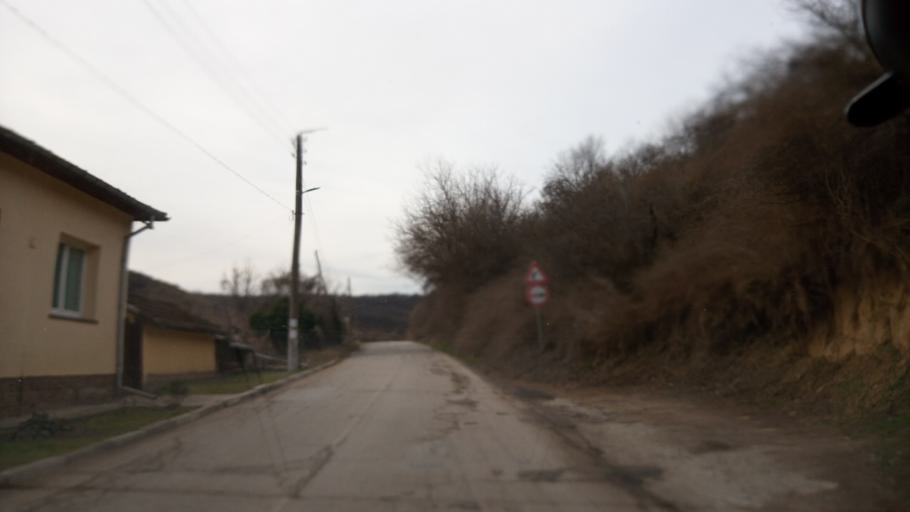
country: BG
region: Pleven
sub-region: Obshtina Belene
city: Belene
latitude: 43.5995
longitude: 24.9951
